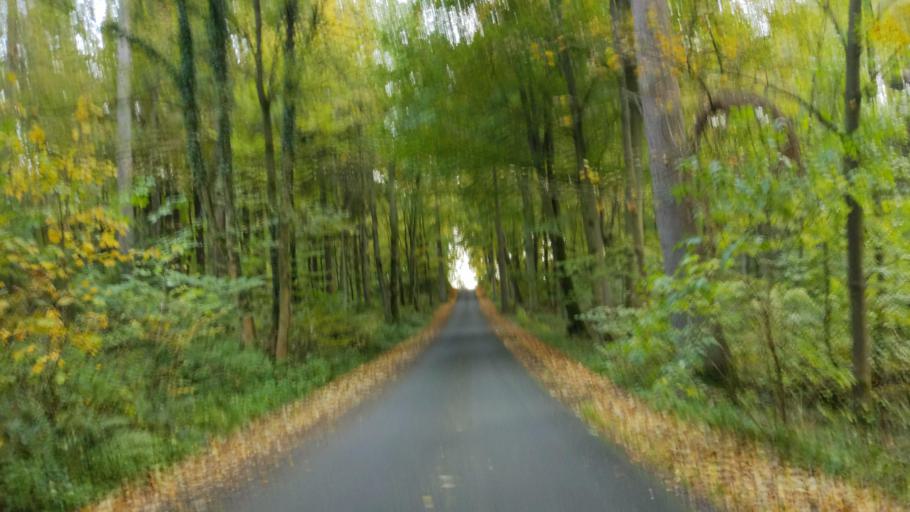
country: DE
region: Schleswig-Holstein
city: Kasseedorf
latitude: 54.1447
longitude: 10.6974
